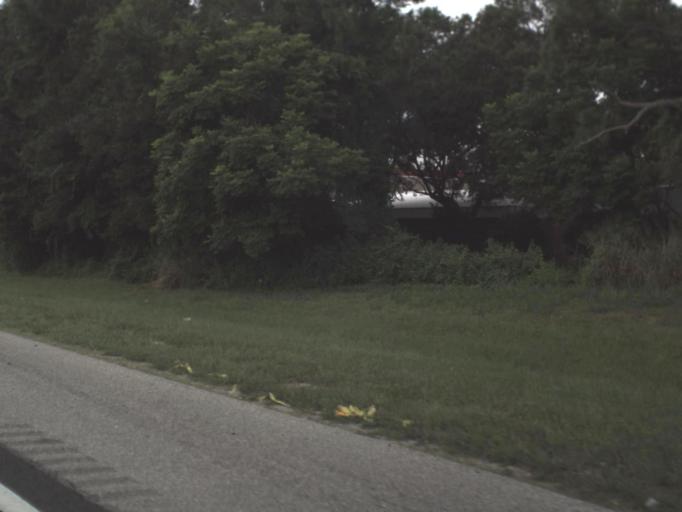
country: US
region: Florida
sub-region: Sarasota County
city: Fruitville
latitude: 27.3158
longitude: -82.4482
